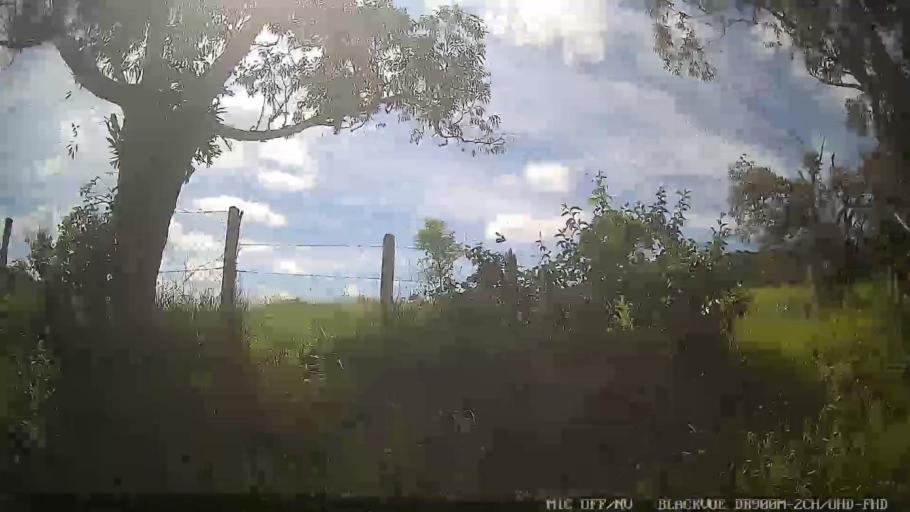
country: BR
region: Sao Paulo
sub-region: Braganca Paulista
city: Braganca Paulista
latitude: -22.9700
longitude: -46.6323
